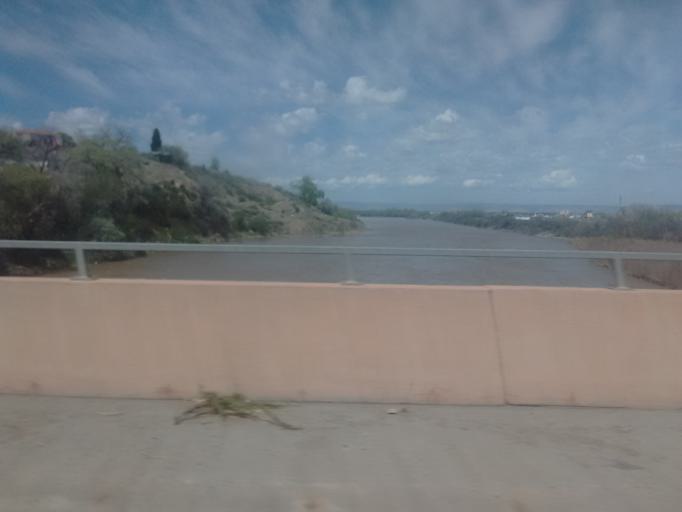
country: US
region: Colorado
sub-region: Mesa County
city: Redlands
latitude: 39.0882
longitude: -108.6252
